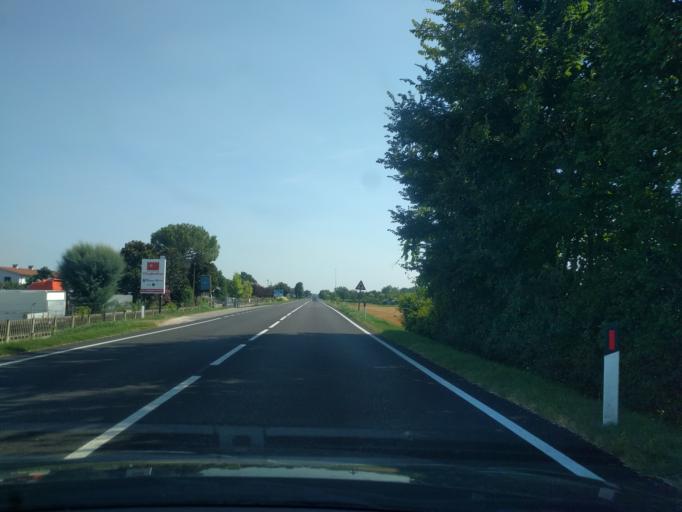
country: IT
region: Veneto
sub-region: Provincia di Padova
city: Solesino
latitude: 45.1948
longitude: 11.7557
